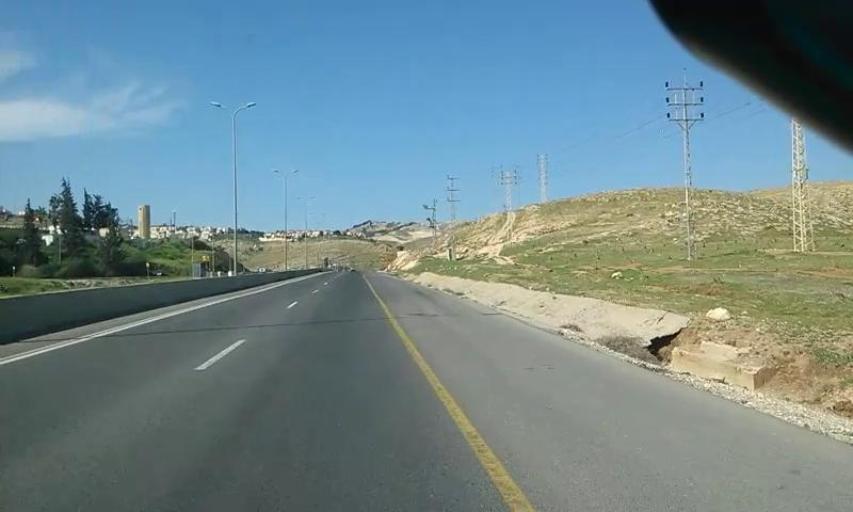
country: PS
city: Az Za`ayyim
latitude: 31.8015
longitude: 35.3184
